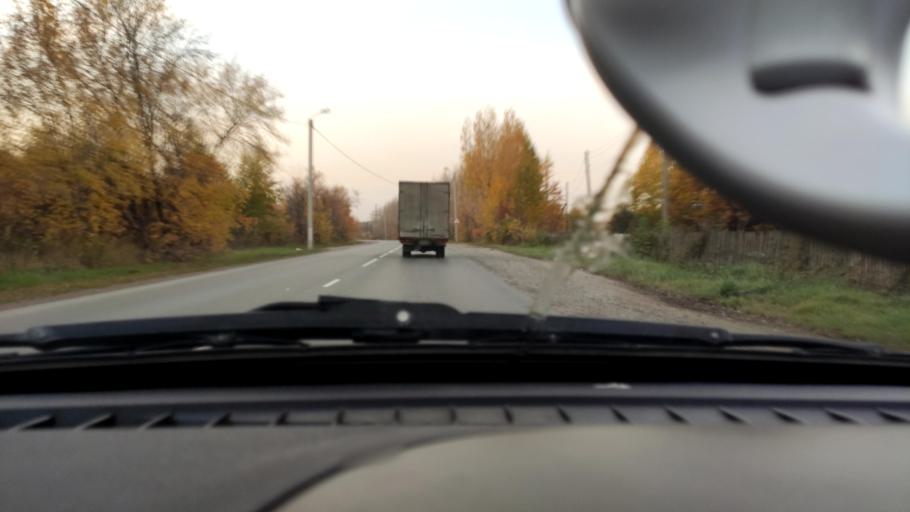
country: RU
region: Perm
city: Kondratovo
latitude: 57.9417
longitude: 56.1544
